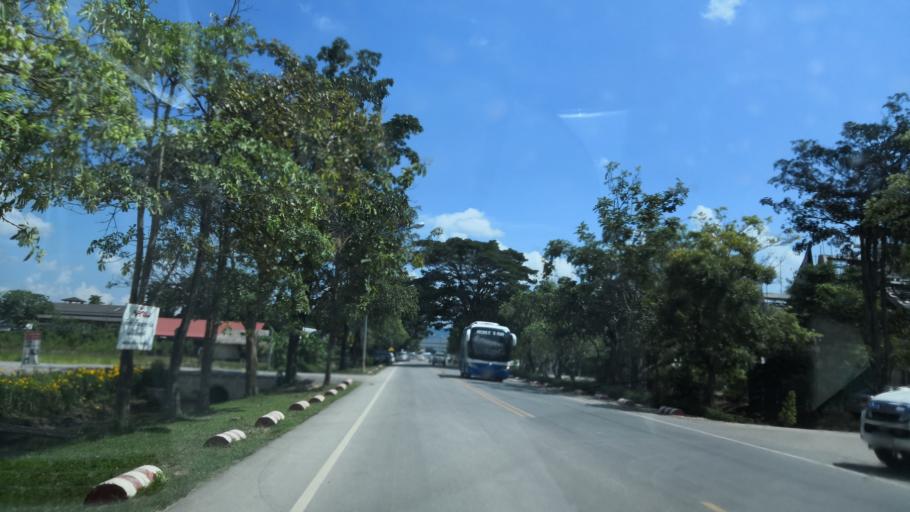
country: TH
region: Chiang Rai
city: Mae Lao
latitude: 19.8251
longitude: 99.7614
